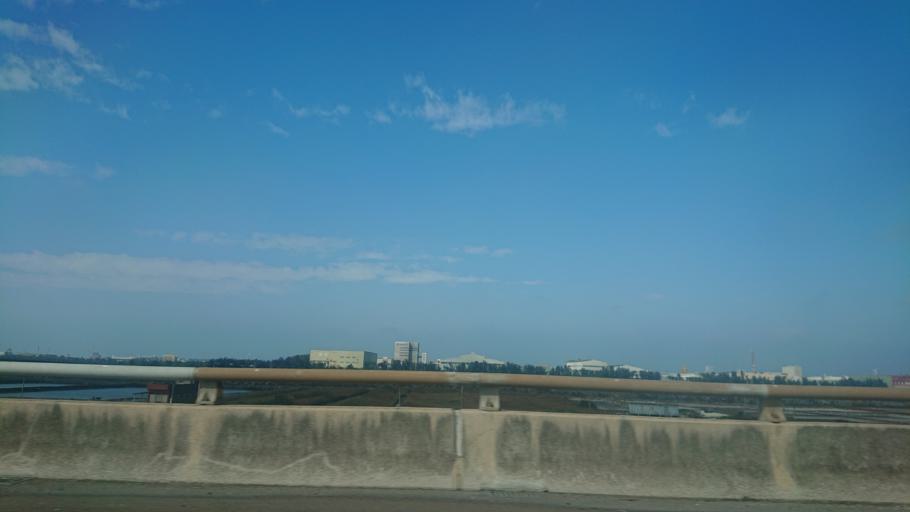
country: TW
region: Taiwan
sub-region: Changhua
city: Chang-hua
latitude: 24.0646
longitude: 120.4116
